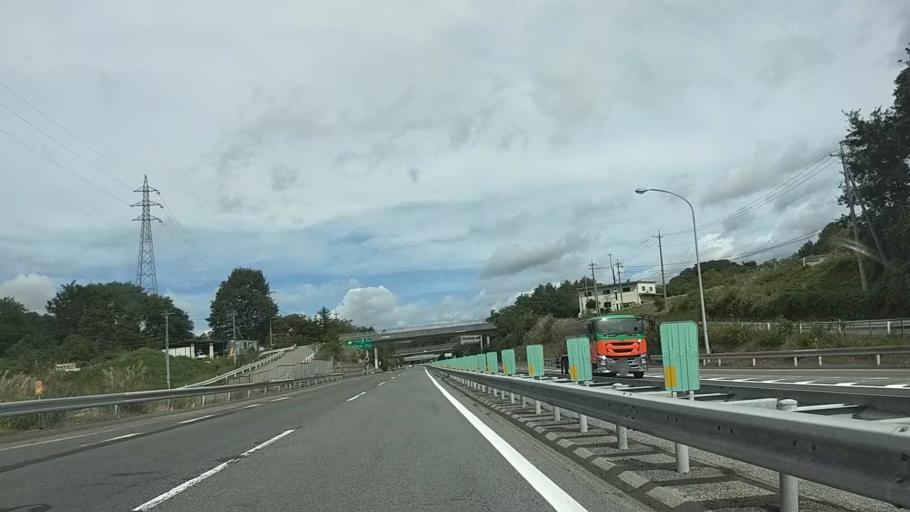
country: JP
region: Nagano
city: Chino
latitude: 35.9379
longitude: 138.2104
